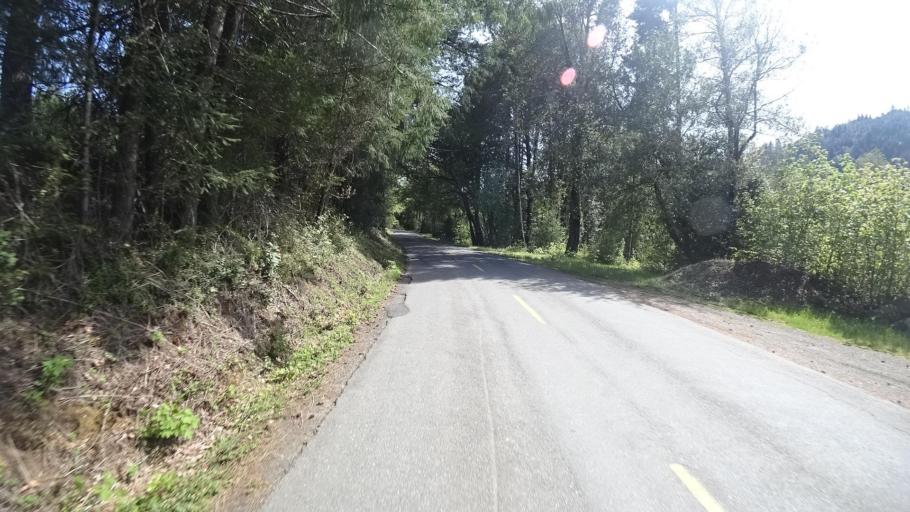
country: US
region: California
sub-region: Humboldt County
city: Redway
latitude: 40.3778
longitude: -123.7427
